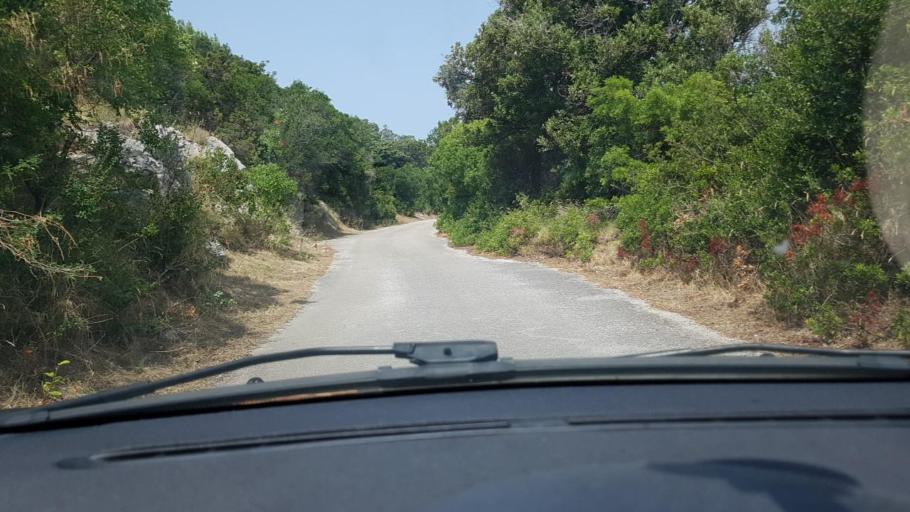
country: ME
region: Herceg Novi
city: Herceg-Novi
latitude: 42.4013
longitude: 18.5185
